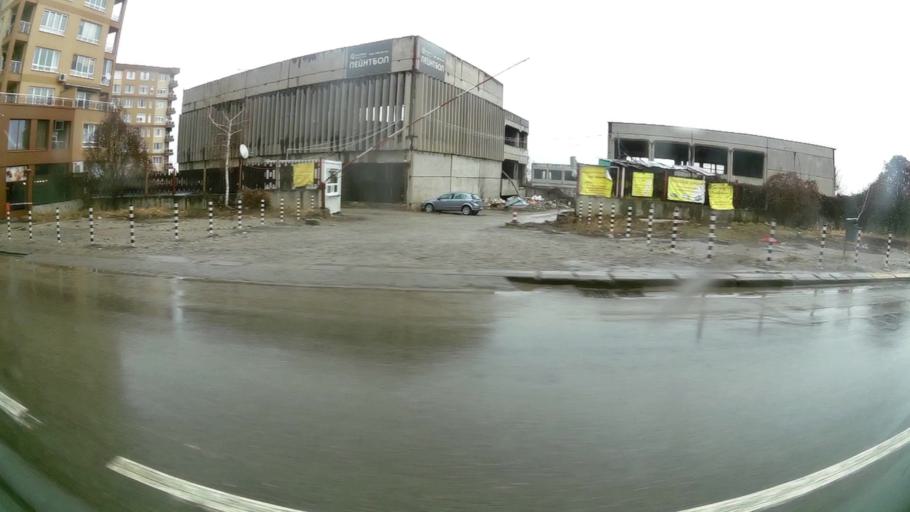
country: BG
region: Sofia-Capital
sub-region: Stolichna Obshtina
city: Sofia
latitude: 42.6261
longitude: 23.3847
